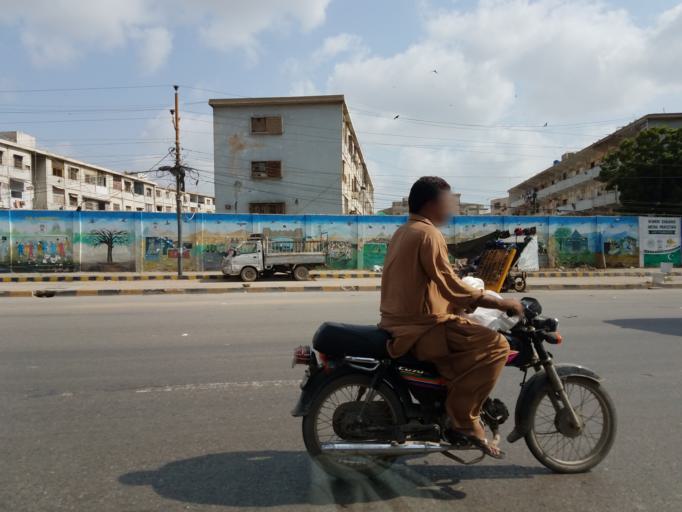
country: PK
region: Sindh
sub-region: Karachi District
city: Karachi
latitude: 24.9219
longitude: 67.0571
